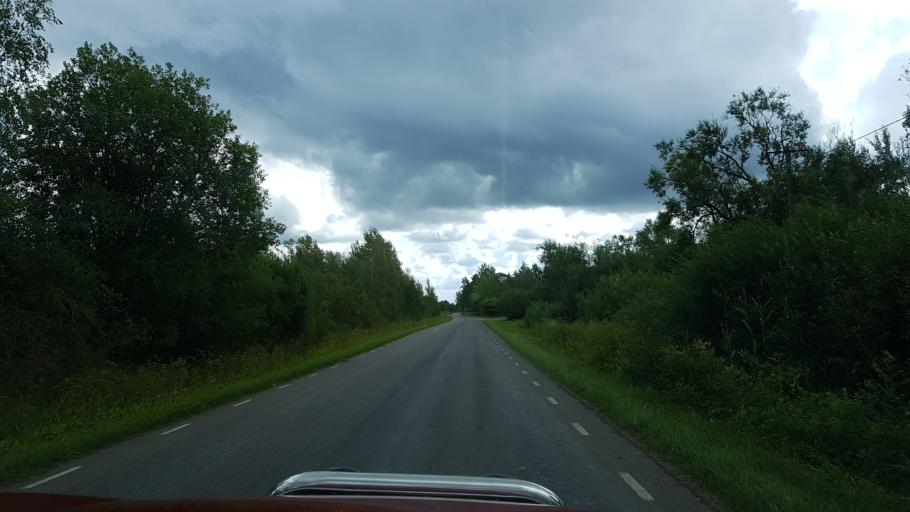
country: EE
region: Laeaene
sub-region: Lihula vald
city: Lihula
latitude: 58.7238
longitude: 23.9559
